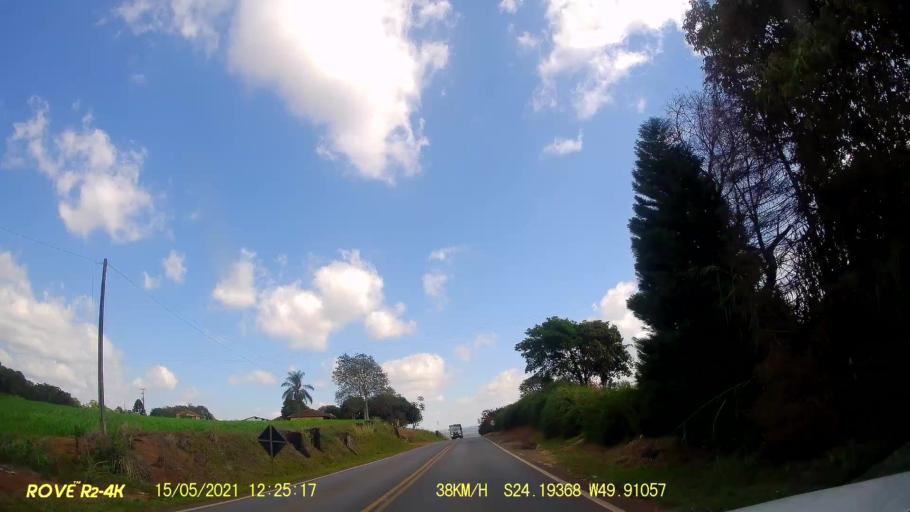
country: BR
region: Parana
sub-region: Jaguariaiva
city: Jaguariaiva
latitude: -24.1937
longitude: -49.9108
